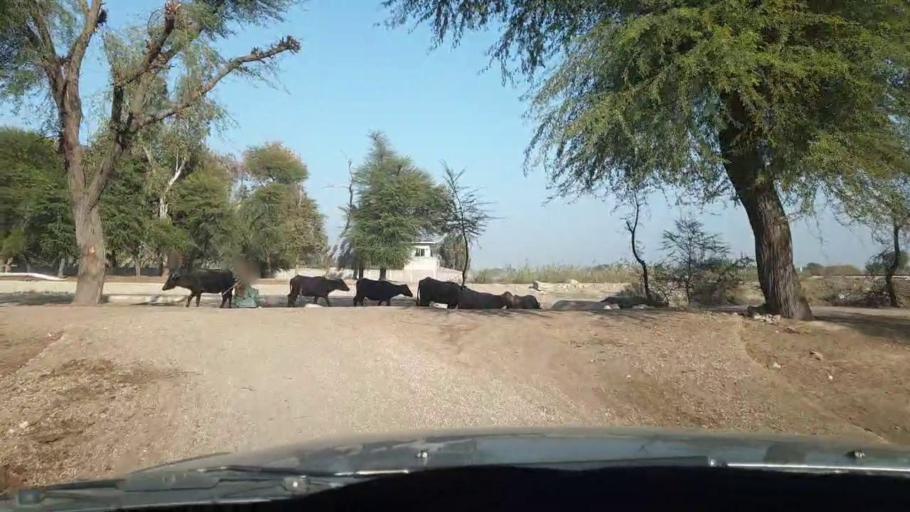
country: PK
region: Sindh
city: Mirpur Mathelo
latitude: 28.0224
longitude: 69.5914
